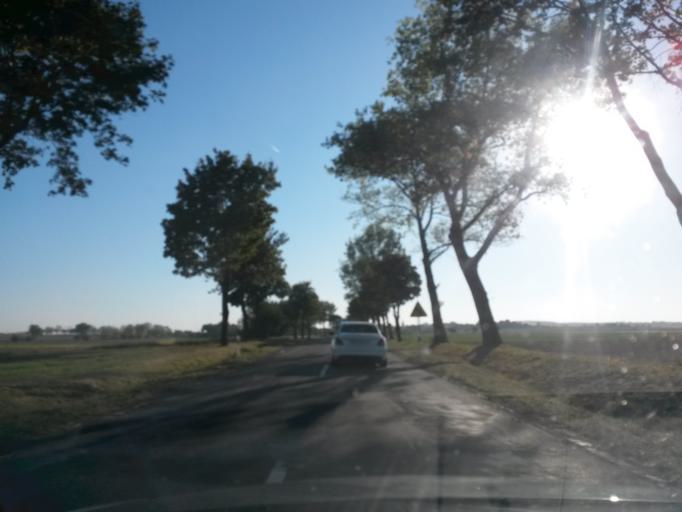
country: PL
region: Lower Silesian Voivodeship
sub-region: Powiat sredzki
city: Udanin
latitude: 51.0495
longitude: 16.4022
